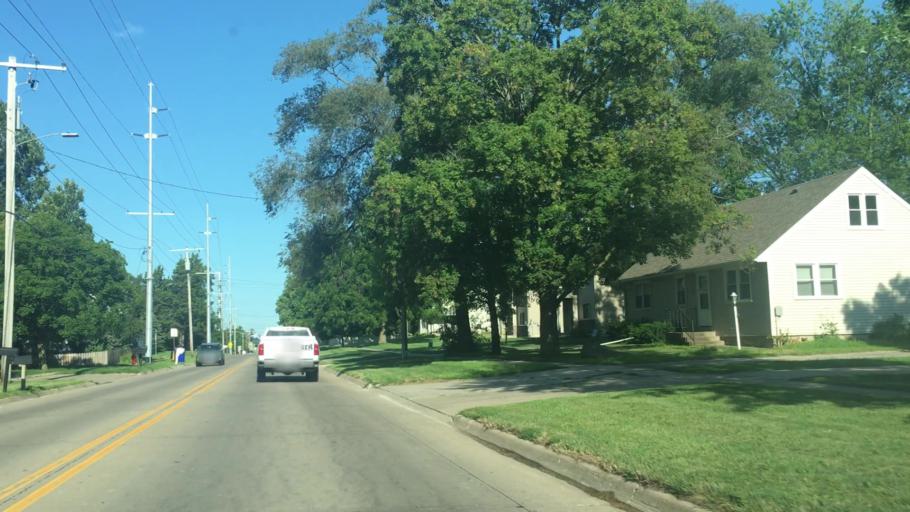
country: US
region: Iowa
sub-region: Johnson County
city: North Liberty
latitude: 41.7521
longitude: -91.5996
